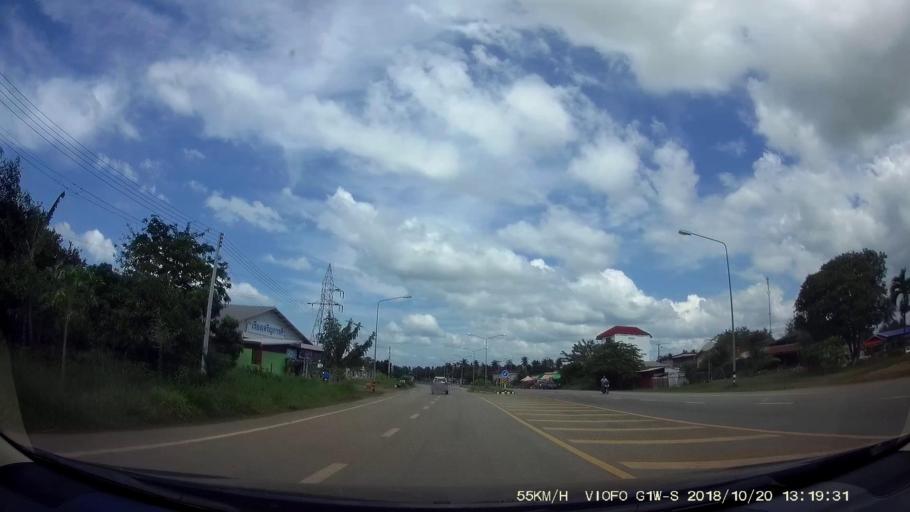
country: TH
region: Chaiyaphum
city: Khon San
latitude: 16.5399
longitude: 101.8996
